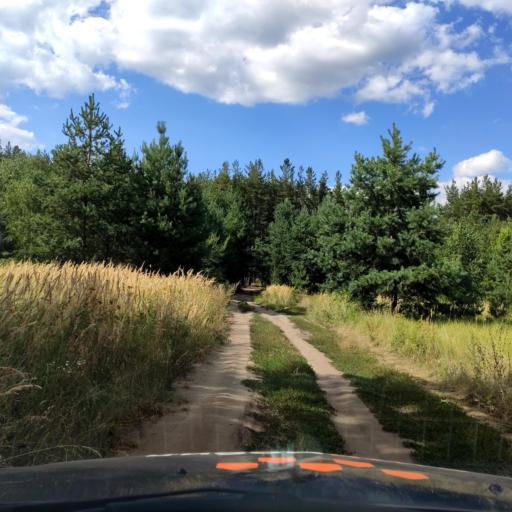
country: RU
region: Voronezj
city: Somovo
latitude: 51.7210
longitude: 39.3983
